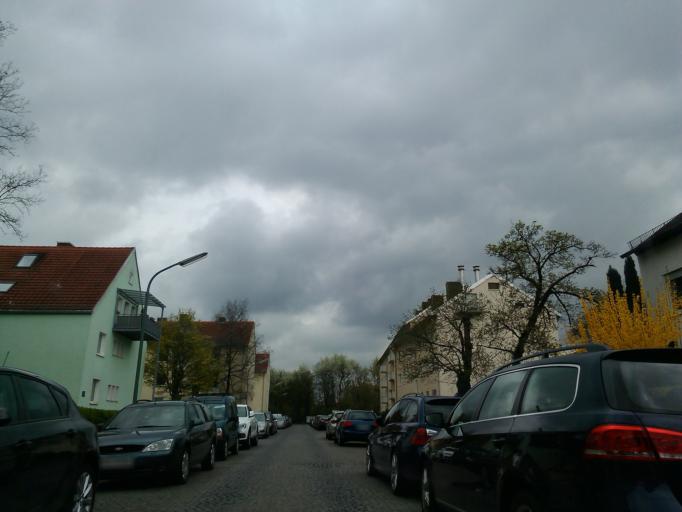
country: DE
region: Bavaria
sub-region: Upper Bavaria
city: Pasing
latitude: 48.1391
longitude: 11.4980
